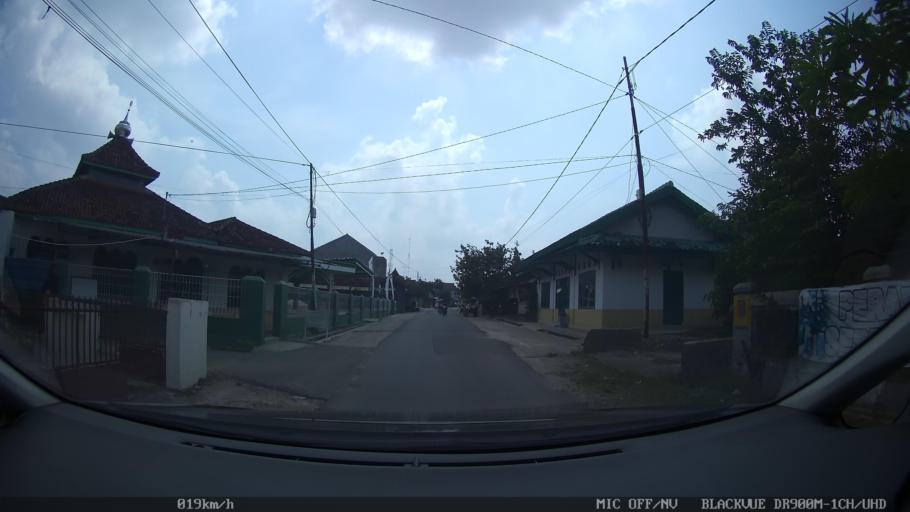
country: ID
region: Lampung
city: Pringsewu
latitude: -5.3581
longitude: 104.9702
